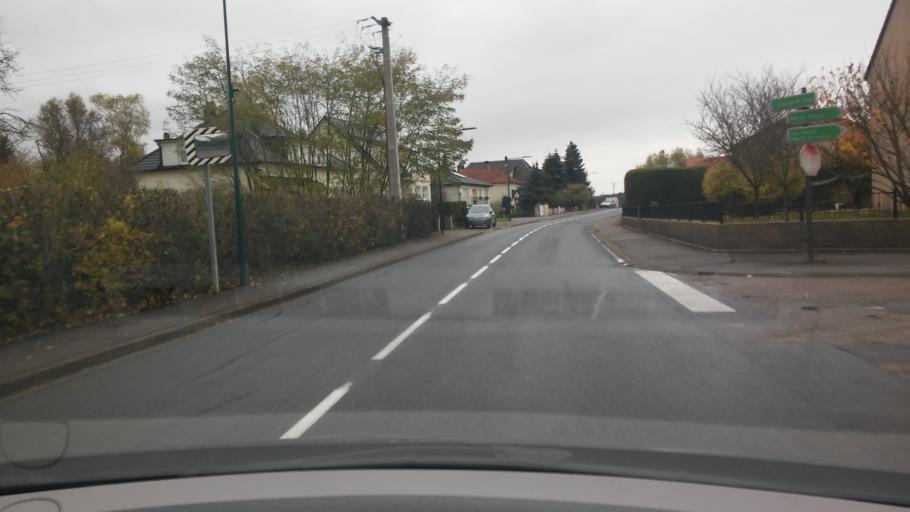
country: FR
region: Lorraine
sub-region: Departement de la Moselle
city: Rurange-les-Thionville
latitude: 49.2772
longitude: 6.2338
